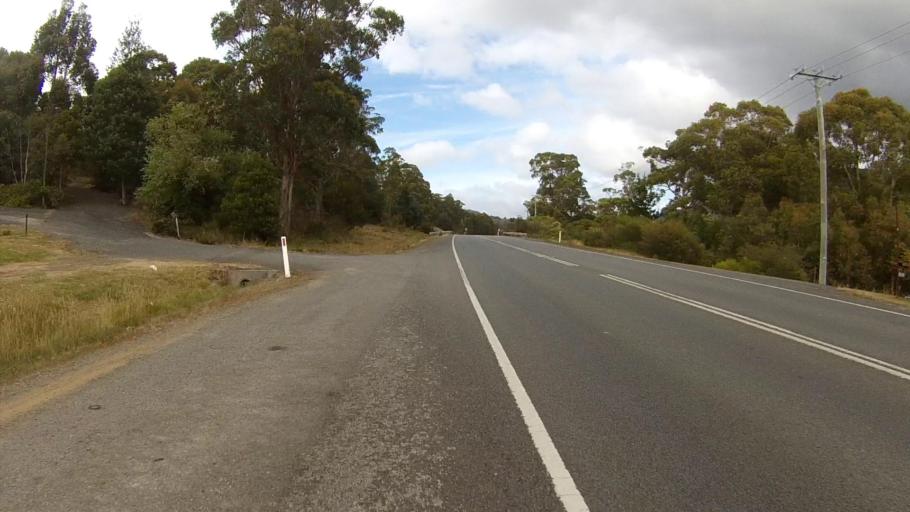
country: AU
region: Tasmania
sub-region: Kingborough
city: Kettering
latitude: -43.0782
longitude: 147.2561
